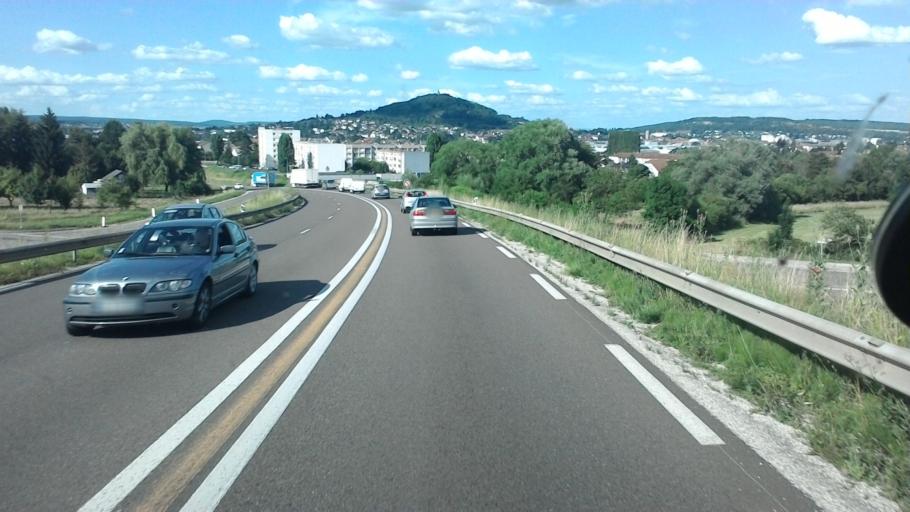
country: FR
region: Franche-Comte
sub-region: Departement de la Haute-Saone
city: Noidans-les-Vesoul
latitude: 47.6089
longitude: 6.1316
